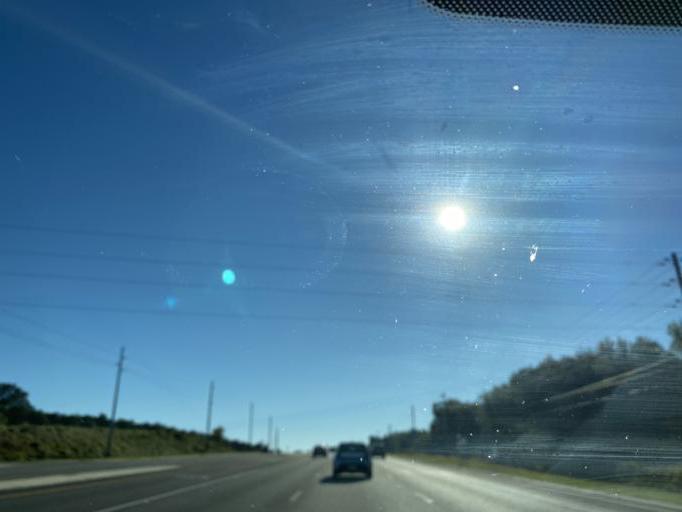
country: US
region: Florida
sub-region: Lake County
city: Clermont
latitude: 28.4713
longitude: -81.7169
